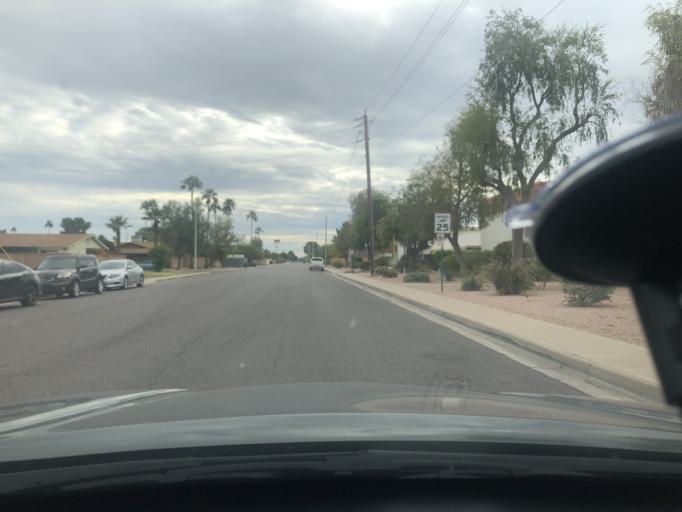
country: US
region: Arizona
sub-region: Maricopa County
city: Scottsdale
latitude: 33.4942
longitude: -111.9003
